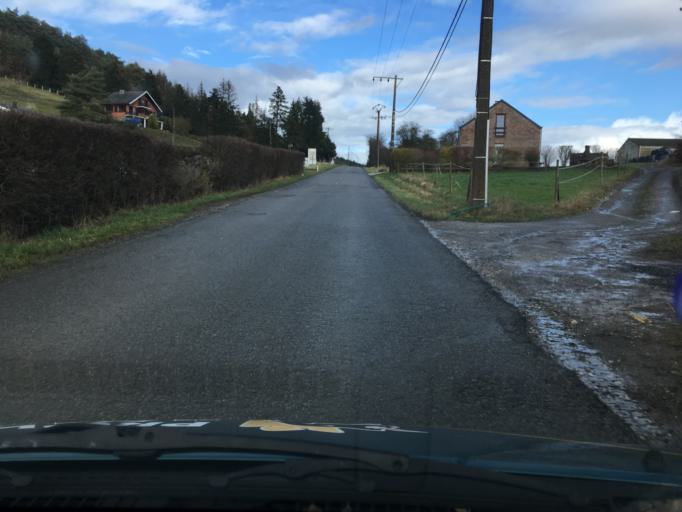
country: FR
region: Champagne-Ardenne
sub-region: Departement des Ardennes
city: Vireux-Molhain
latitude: 50.0952
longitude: 4.6769
